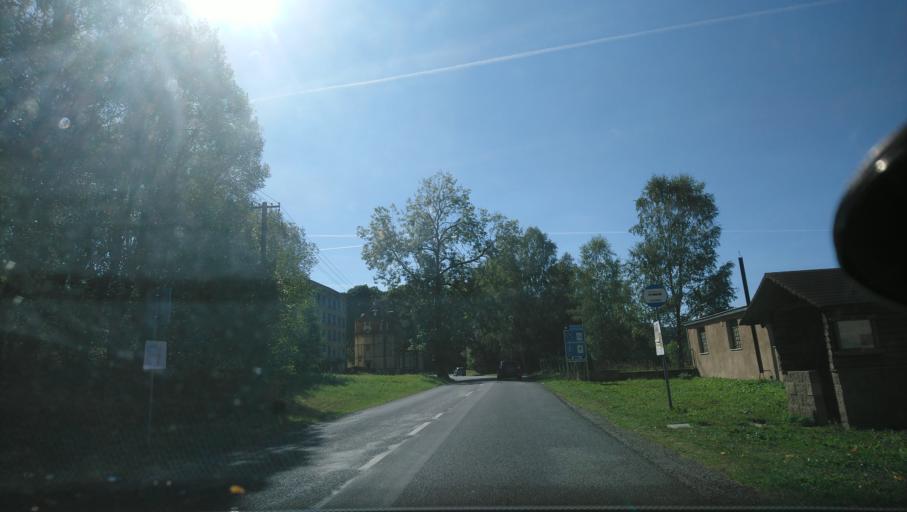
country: CZ
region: Ustecky
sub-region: Okres Chomutov
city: Vejprty
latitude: 50.4826
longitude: 13.0251
